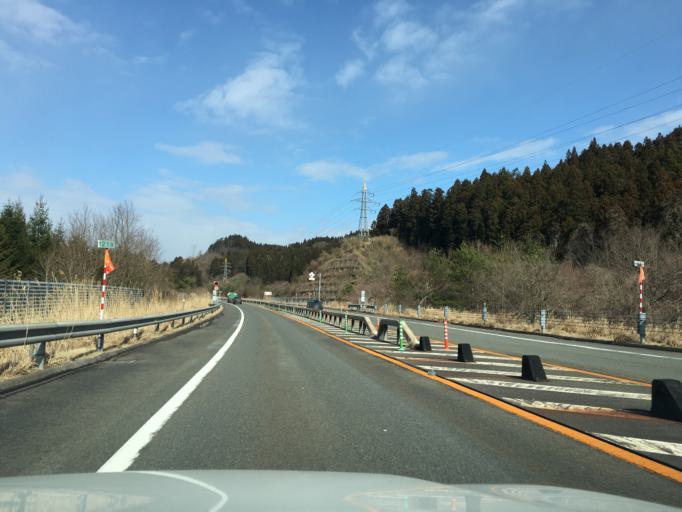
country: JP
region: Akita
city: Akita
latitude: 39.7741
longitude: 140.1199
